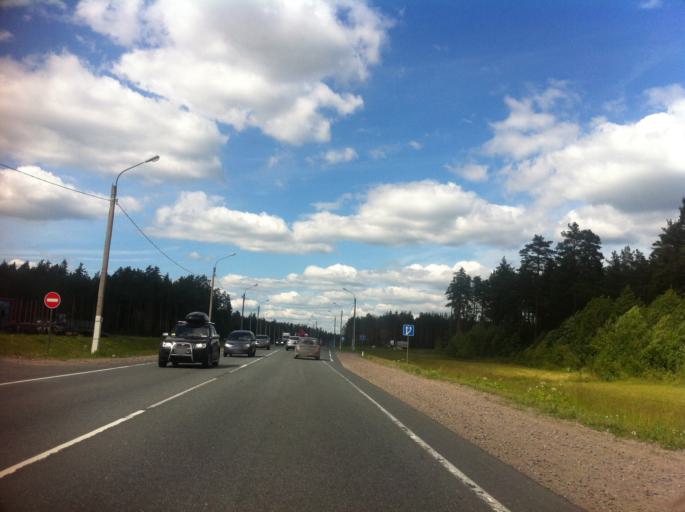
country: RU
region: Leningrad
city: Luga
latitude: 58.7128
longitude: 29.8793
